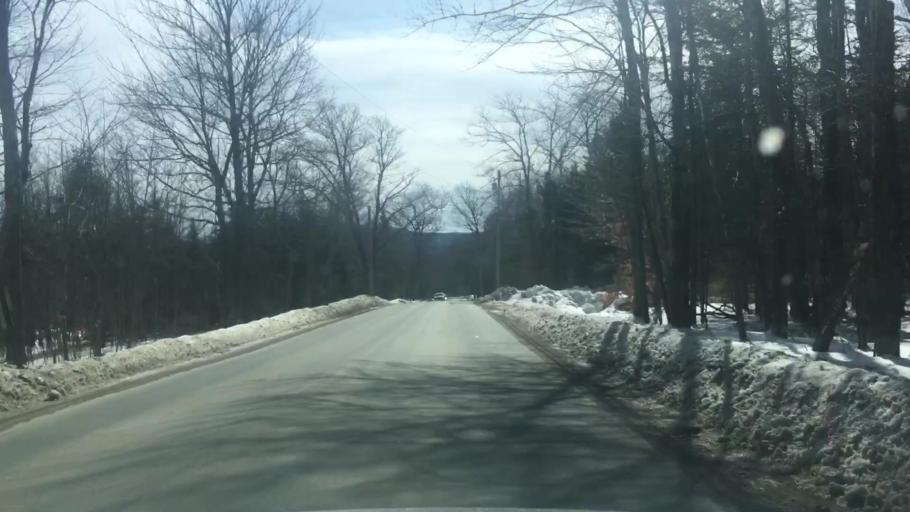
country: US
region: Maine
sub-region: Penobscot County
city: Holden
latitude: 44.7623
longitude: -68.6420
